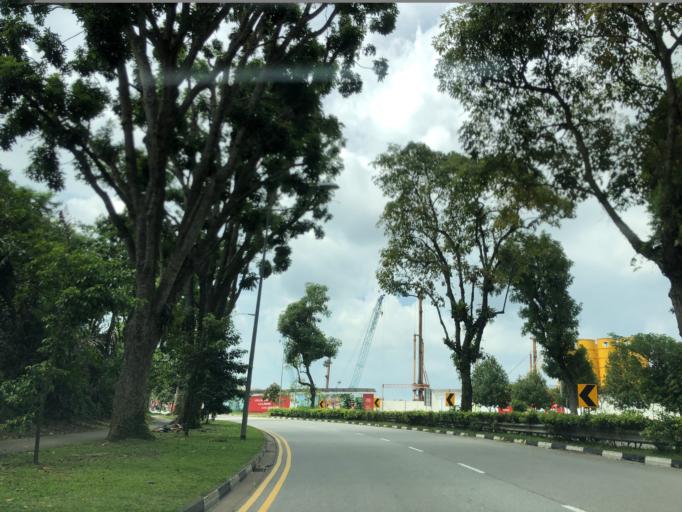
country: MY
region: Johor
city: Kampung Pasir Gudang Baru
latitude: 1.4262
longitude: 103.8550
